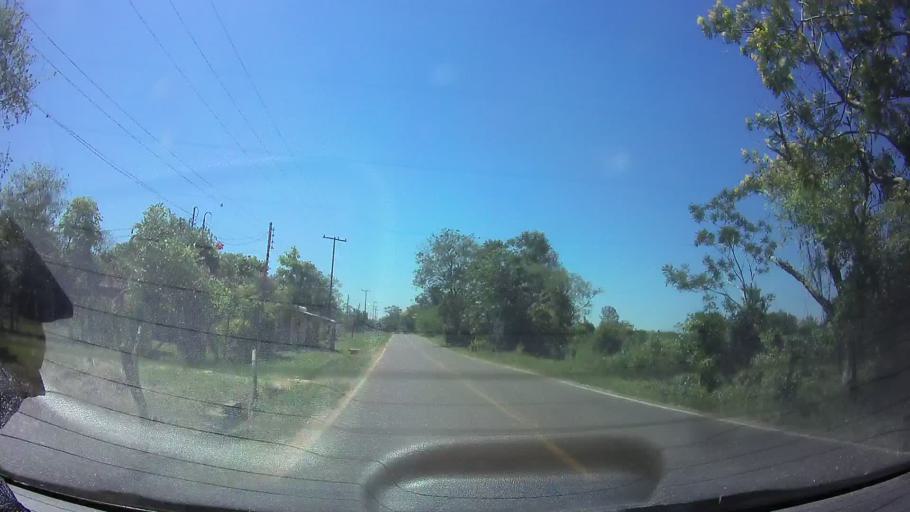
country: PY
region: Central
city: Aregua
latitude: -25.2671
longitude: -57.4123
